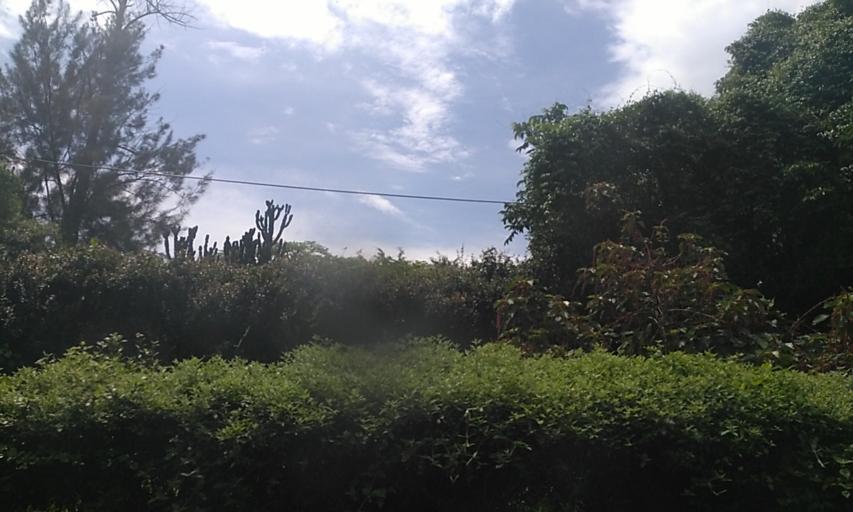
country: UG
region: Central Region
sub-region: Kampala District
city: Kampala
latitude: 0.3287
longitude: 32.6021
